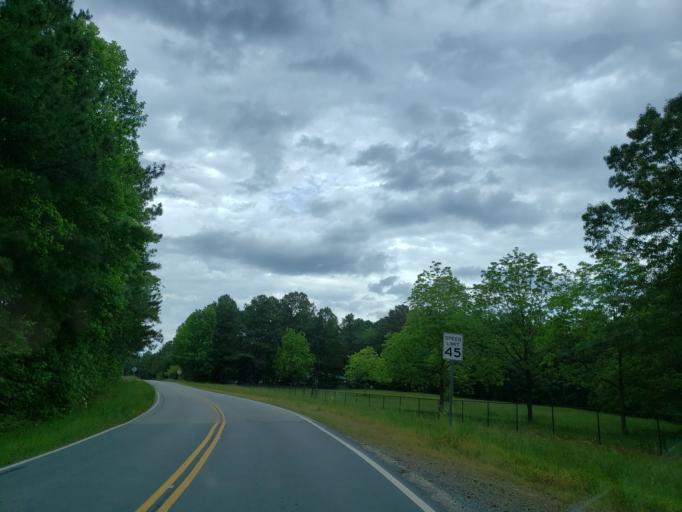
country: US
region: Georgia
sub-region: Polk County
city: Rockmart
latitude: 33.9380
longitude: -85.0439
